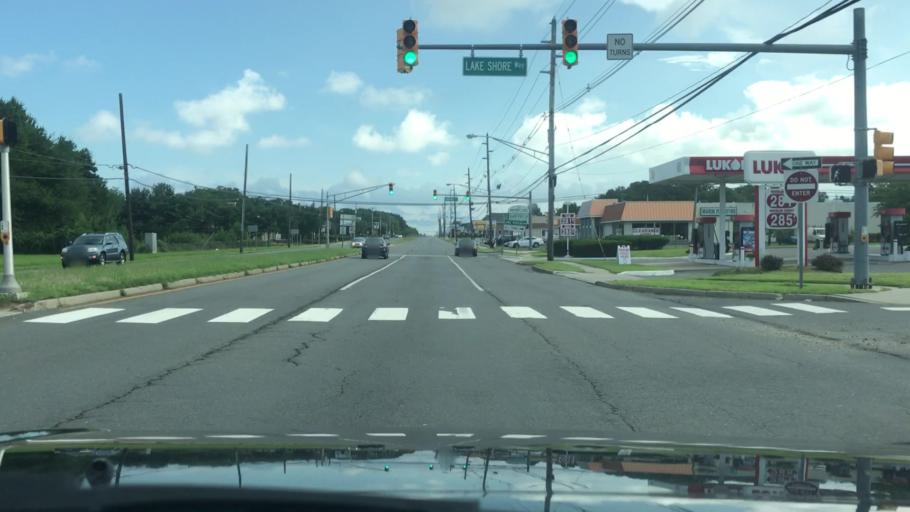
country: US
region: New Jersey
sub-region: Ocean County
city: Leisure Village East
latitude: 40.0409
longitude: -74.1425
